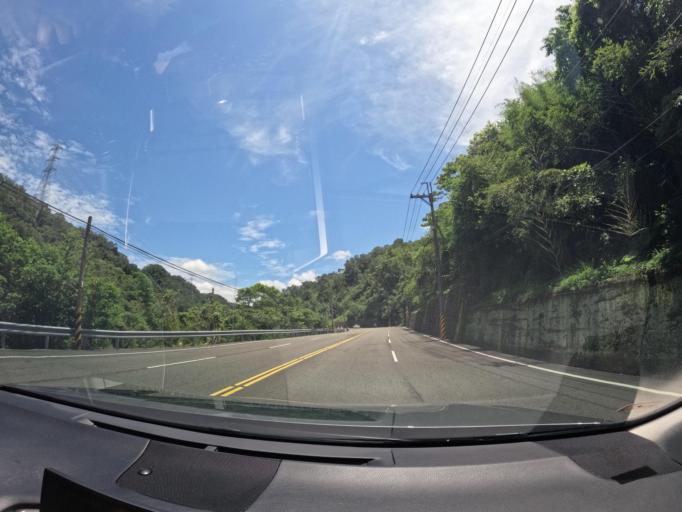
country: TW
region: Taiwan
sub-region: Miaoli
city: Miaoli
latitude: 24.5826
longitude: 120.9424
